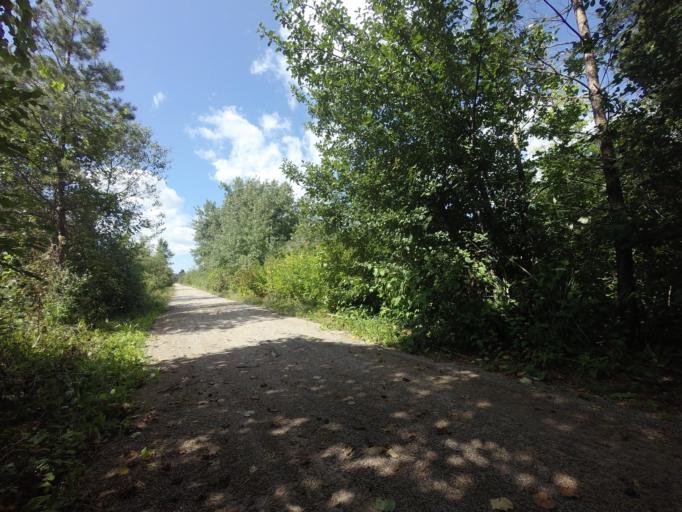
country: CA
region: Ontario
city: Huron East
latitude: 43.6554
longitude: -81.2392
